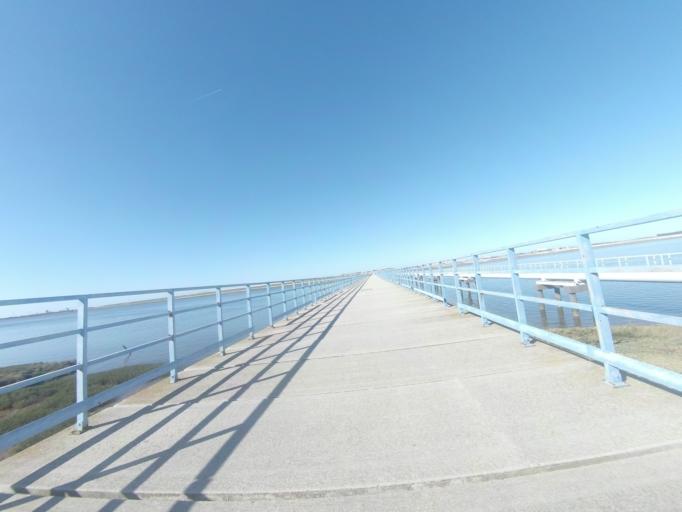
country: ES
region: Andalusia
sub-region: Provincia de Huelva
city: Palos de la Frontera
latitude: 37.2477
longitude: -6.8956
